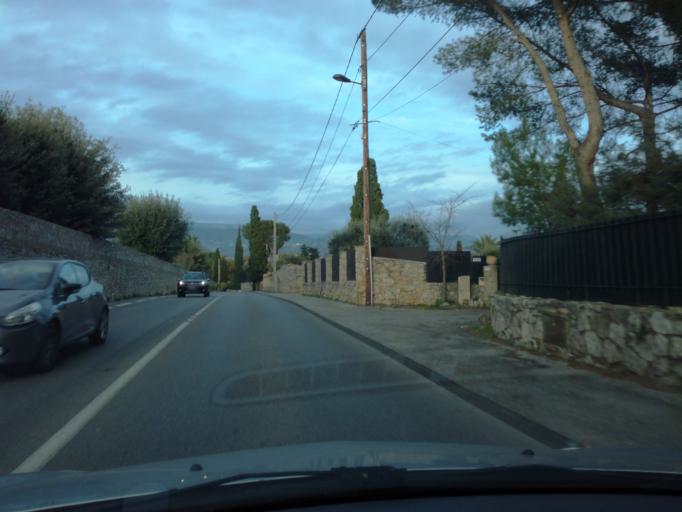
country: FR
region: Provence-Alpes-Cote d'Azur
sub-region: Departement des Alpes-Maritimes
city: Pegomas
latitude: 43.6311
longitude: 6.9388
